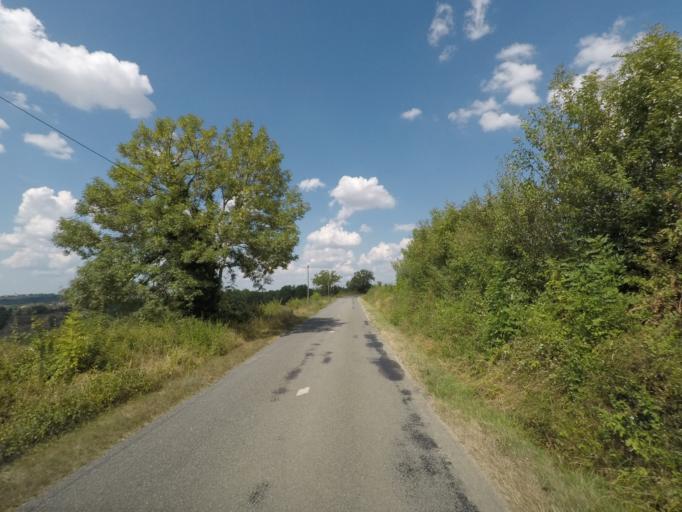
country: FR
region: Midi-Pyrenees
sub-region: Departement du Lot
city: Le Vigan
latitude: 44.6178
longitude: 1.5984
